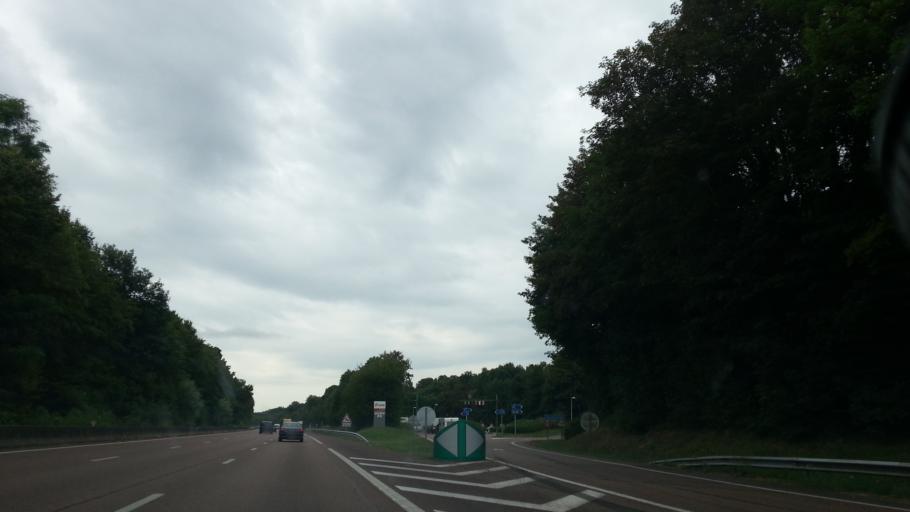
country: FR
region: Bourgogne
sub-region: Departement de Saone-et-Loire
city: Champforgeuil
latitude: 46.8637
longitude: 4.8210
